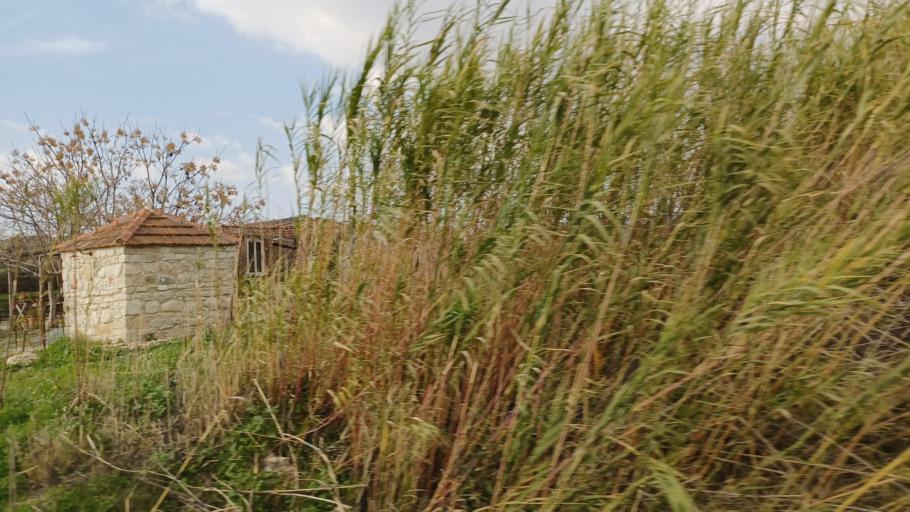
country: CY
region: Limassol
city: Pissouri
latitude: 34.6779
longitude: 32.7595
